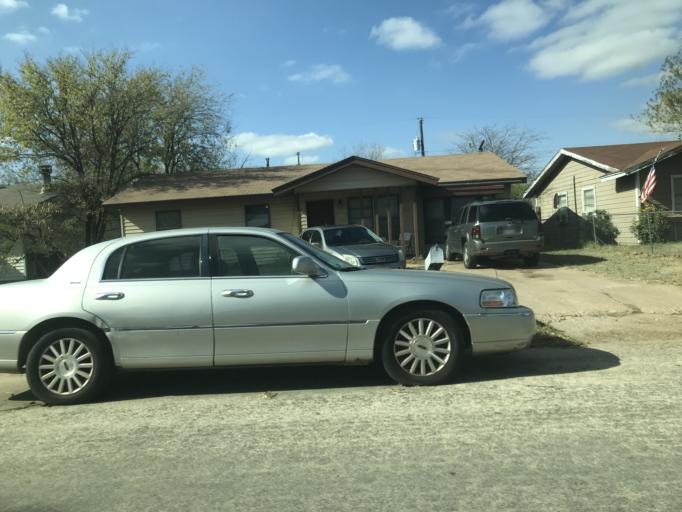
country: US
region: Texas
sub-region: Taylor County
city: Abilene
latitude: 32.4614
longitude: -99.7807
